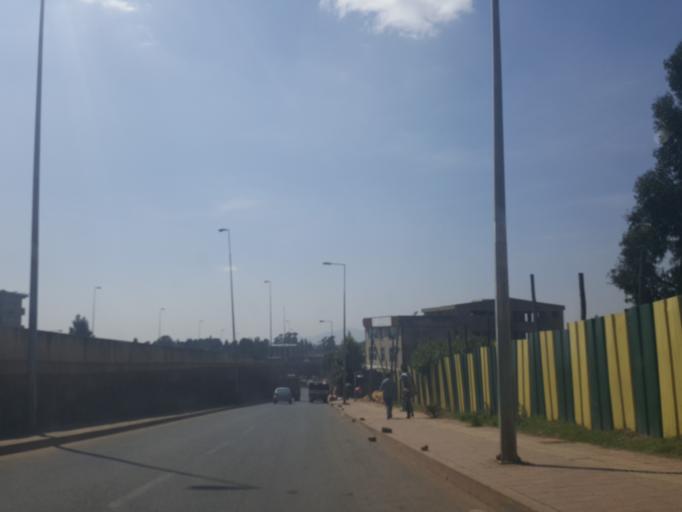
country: ET
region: Adis Abeba
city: Addis Ababa
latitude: 9.0617
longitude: 38.7144
